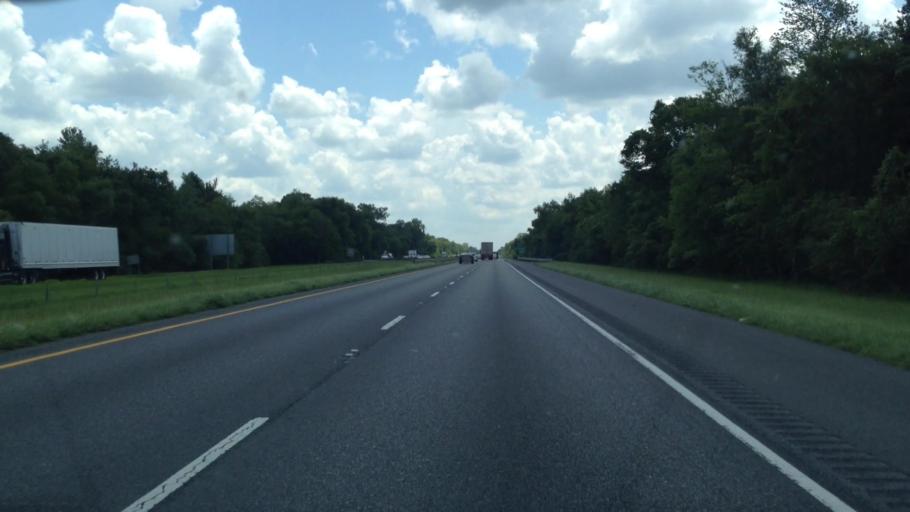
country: US
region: Louisiana
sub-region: Saint James Parish
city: Grand Point
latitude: 30.1446
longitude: -90.7631
